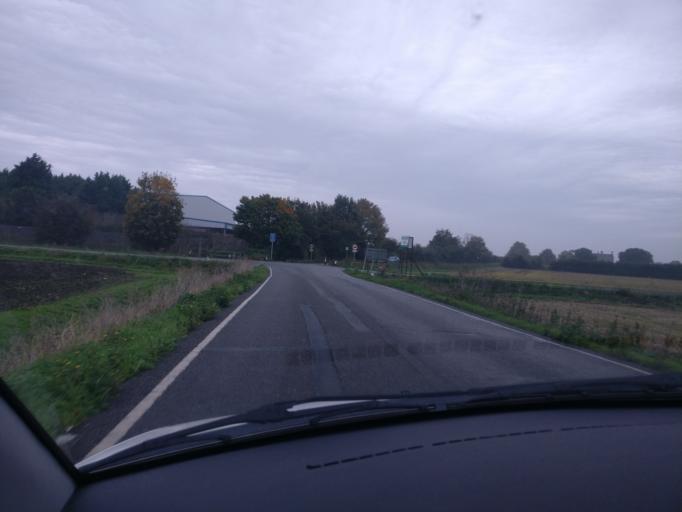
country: GB
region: England
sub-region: Peterborough
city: Eye
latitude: 52.5890
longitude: -0.1939
